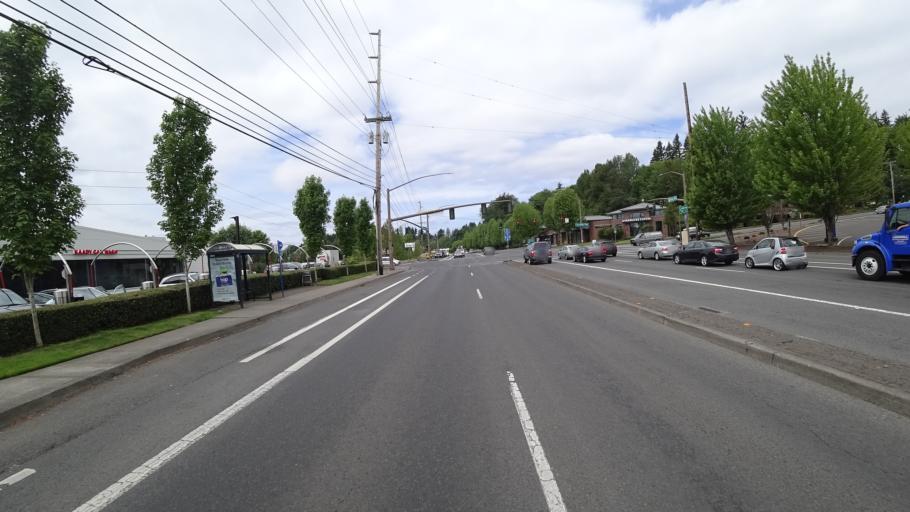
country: US
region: Oregon
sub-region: Clackamas County
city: Milwaukie
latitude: 45.4710
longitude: -122.6848
